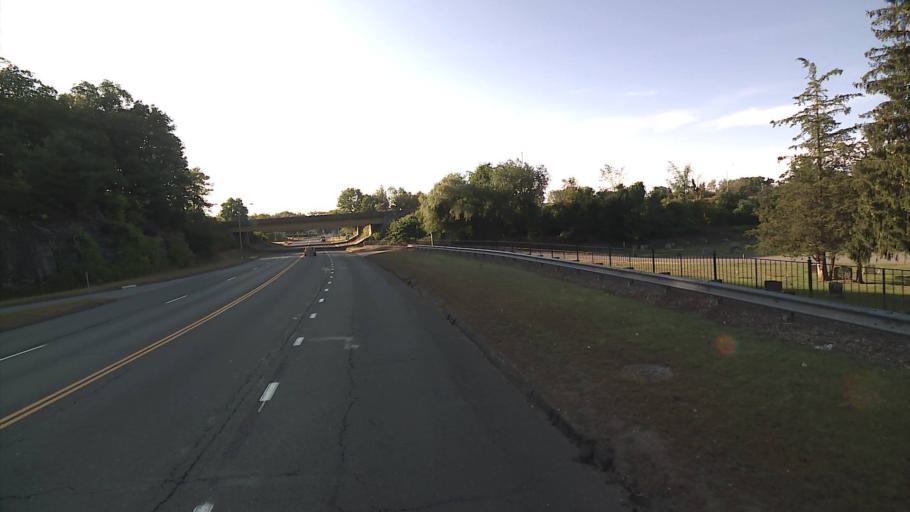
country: US
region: Connecticut
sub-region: Windham County
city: Willimantic
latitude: 41.7270
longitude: -72.2439
